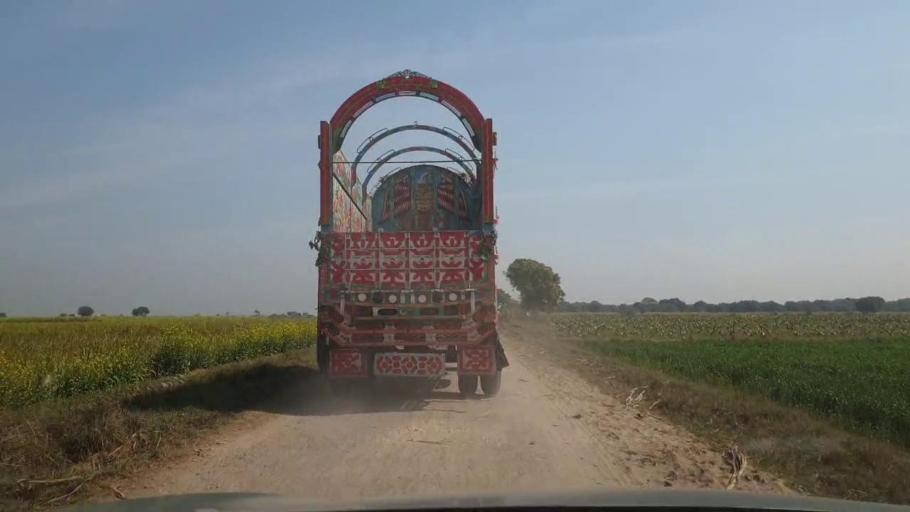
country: PK
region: Sindh
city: Tando Adam
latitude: 25.6284
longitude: 68.7318
